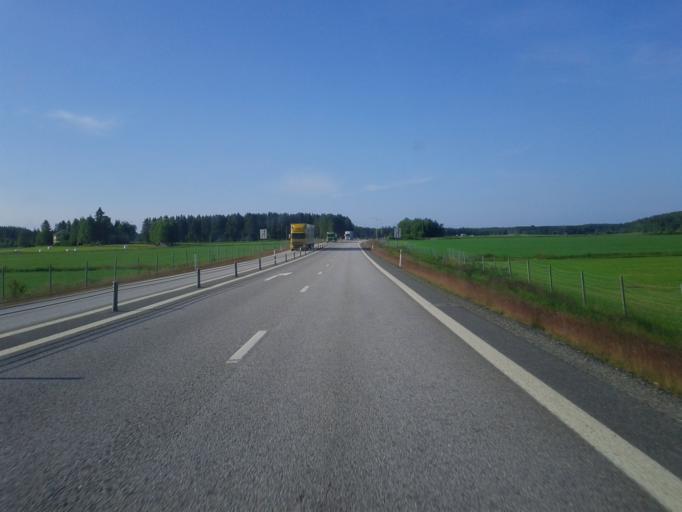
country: SE
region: Vaesterbotten
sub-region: Robertsfors Kommun
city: Robertsfors
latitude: 64.0964
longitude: 20.8697
